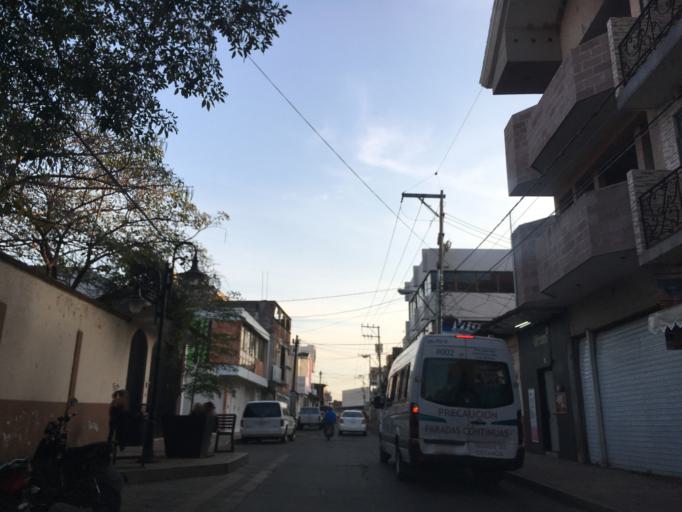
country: MX
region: Michoacan
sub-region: Los Reyes
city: La Higuerita (Colonia San Rafael)
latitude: 19.5887
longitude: -102.4750
